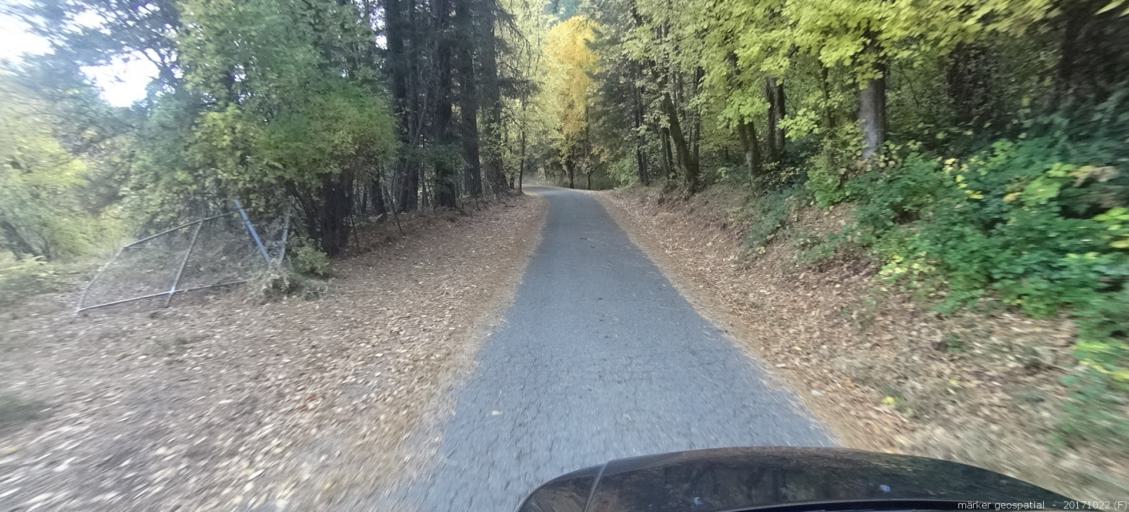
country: US
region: California
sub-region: Siskiyou County
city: Dunsmuir
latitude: 41.1650
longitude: -122.2852
